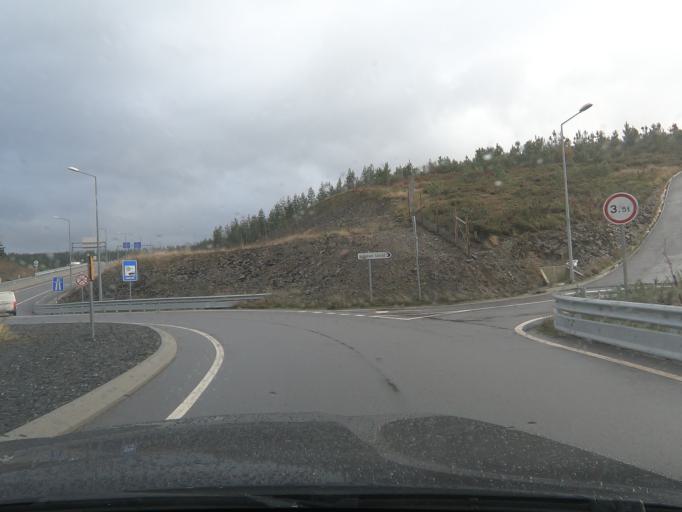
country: PT
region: Vila Real
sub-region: Santa Marta de Penaguiao
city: Santa Marta de Penaguiao
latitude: 41.2826
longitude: -7.8376
